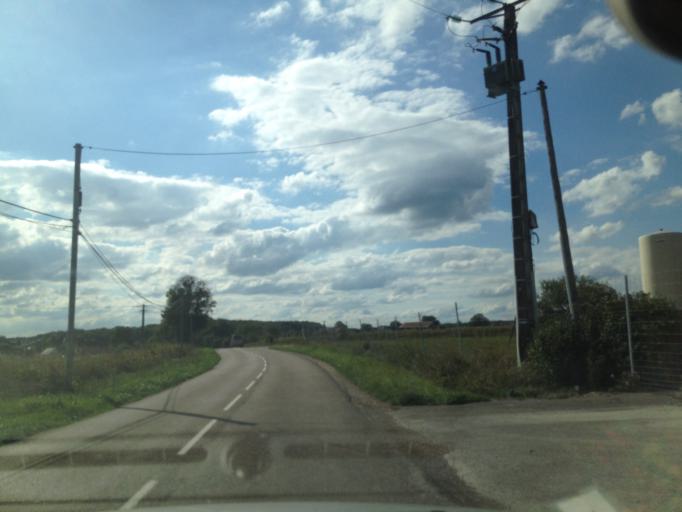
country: FR
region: Franche-Comte
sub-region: Departement de la Haute-Saone
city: Faverney
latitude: 47.8102
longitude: 6.1126
